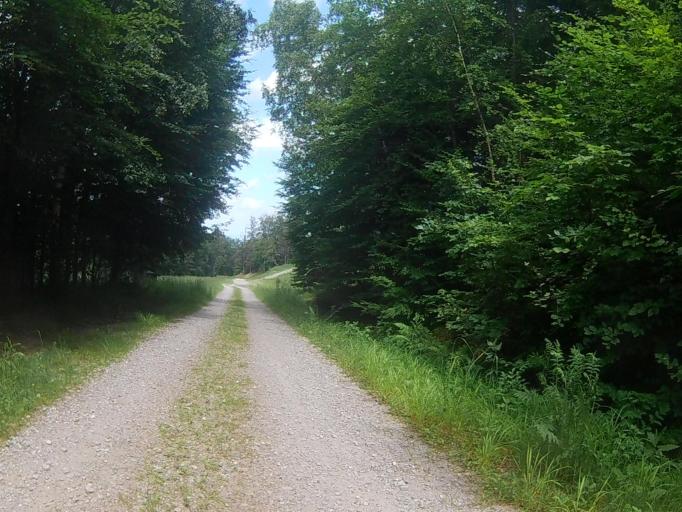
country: SI
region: Ruse
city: Ruse
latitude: 46.5125
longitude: 15.4947
